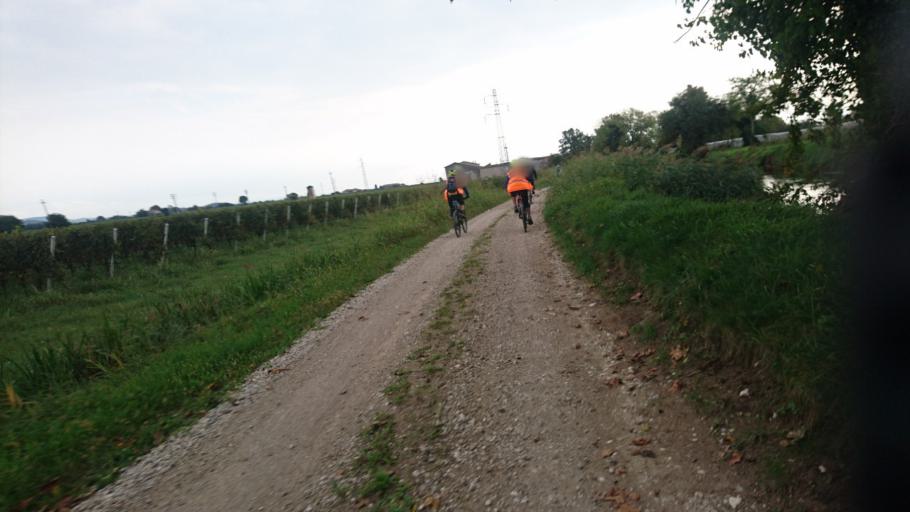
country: IT
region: Veneto
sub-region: Provincia di Verona
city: Monticelli-Fontana
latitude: 45.4025
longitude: 11.1301
